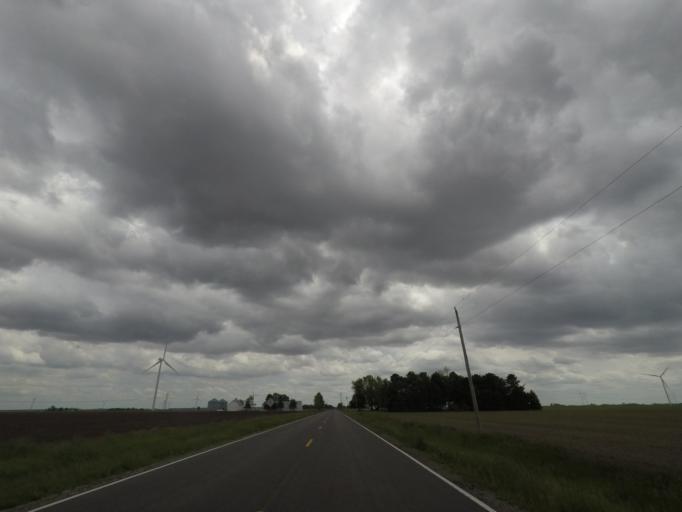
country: US
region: Illinois
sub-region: Macon County
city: Warrensburg
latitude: 40.0041
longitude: -89.0856
